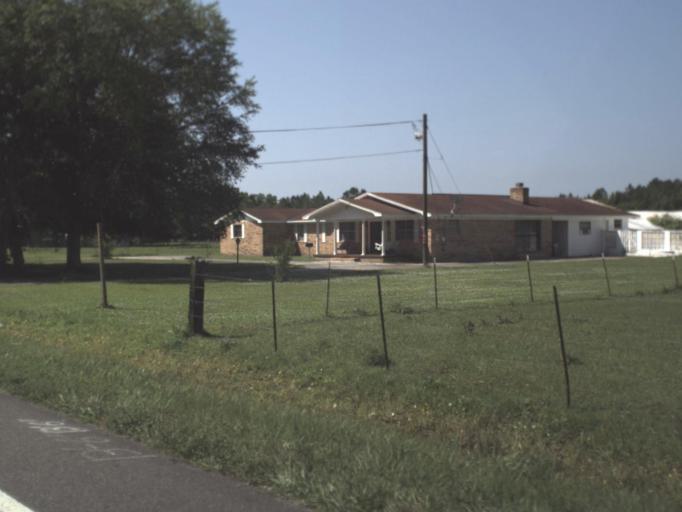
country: US
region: Florida
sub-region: Nassau County
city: Nassau Village-Ratliff
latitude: 30.4818
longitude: -81.7182
